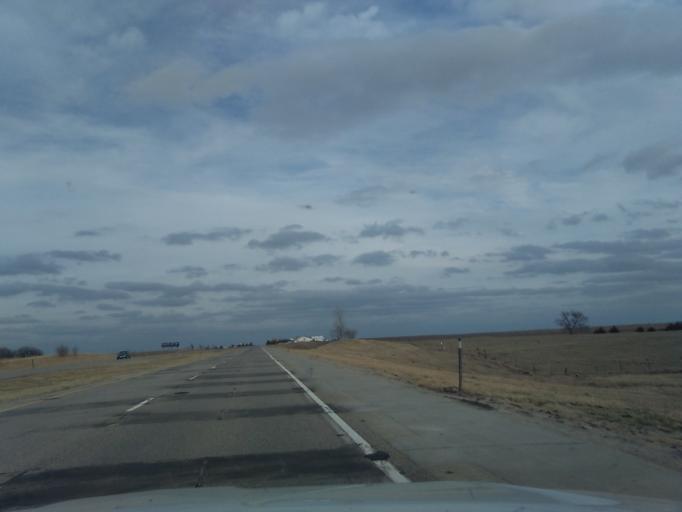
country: US
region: Nebraska
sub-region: Lancaster County
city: Hickman
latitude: 40.4654
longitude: -96.7207
